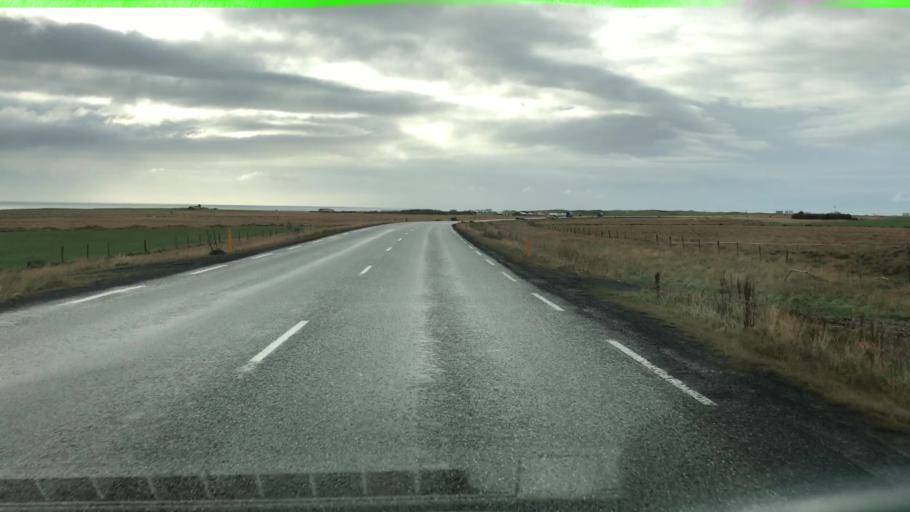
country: IS
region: West
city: Akranes
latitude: 64.3097
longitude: -21.9688
